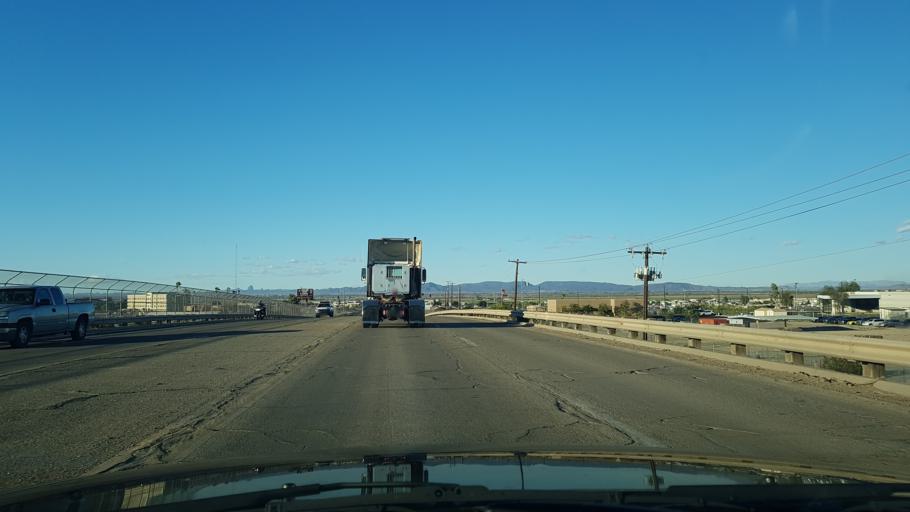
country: US
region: Arizona
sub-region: Yuma County
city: Yuma
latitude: 32.6883
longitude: -114.5988
